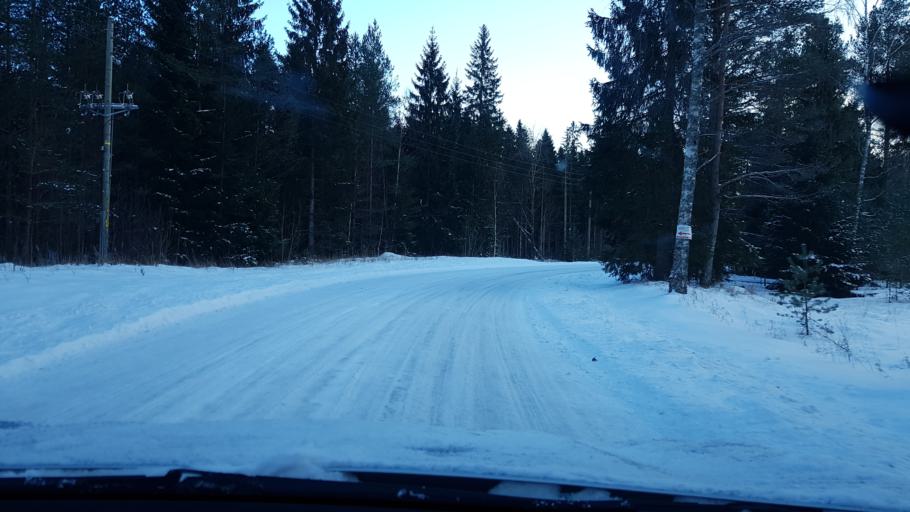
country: EE
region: Harju
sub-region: Nissi vald
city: Turba
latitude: 59.2159
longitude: 24.1409
